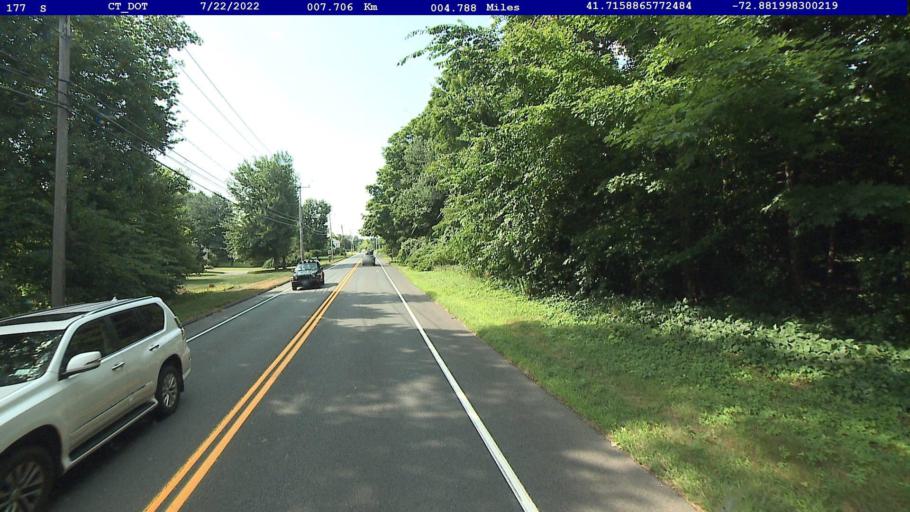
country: US
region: Connecticut
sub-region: Hartford County
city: Plainville
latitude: 41.7159
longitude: -72.8820
